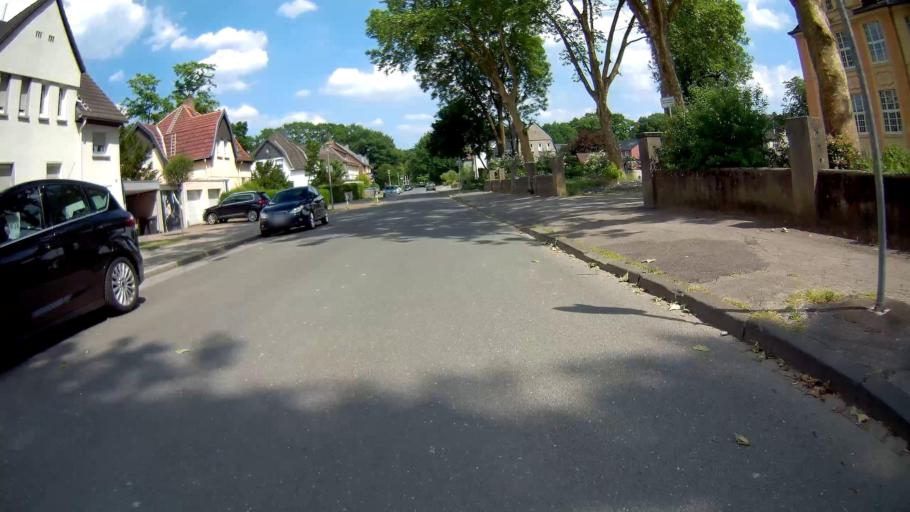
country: DE
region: North Rhine-Westphalia
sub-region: Regierungsbezirk Munster
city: Gladbeck
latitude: 51.5885
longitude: 6.9824
